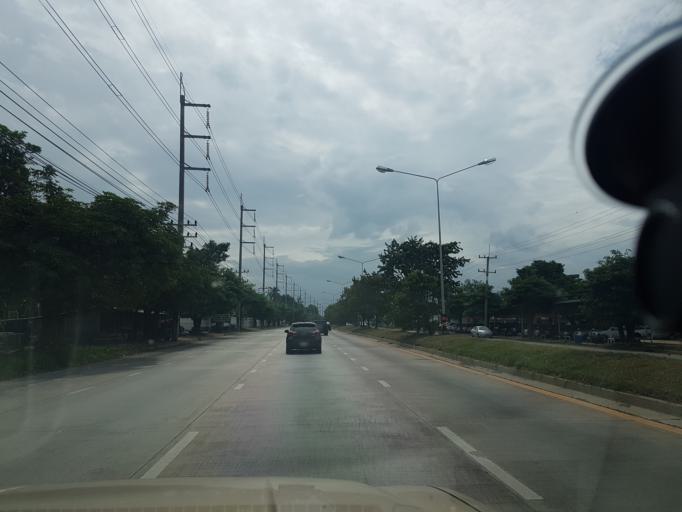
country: TH
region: Sara Buri
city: Phra Phutthabat
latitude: 14.7150
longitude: 100.8189
